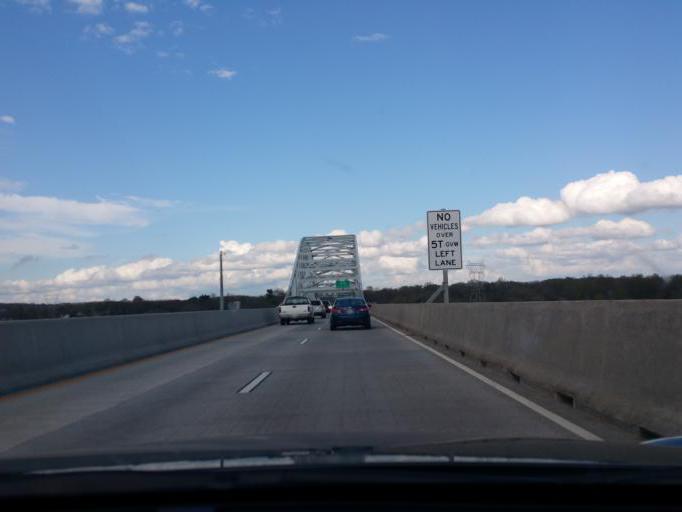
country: US
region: Maryland
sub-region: Cecil County
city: Perryville
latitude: 39.5629
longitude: -76.0850
